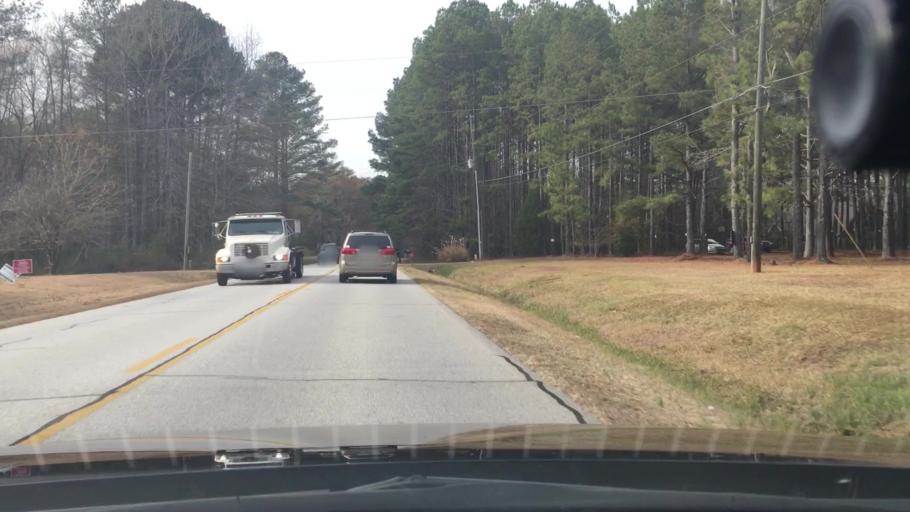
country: US
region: Georgia
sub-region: Coweta County
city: Senoia
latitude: 33.3272
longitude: -84.5024
